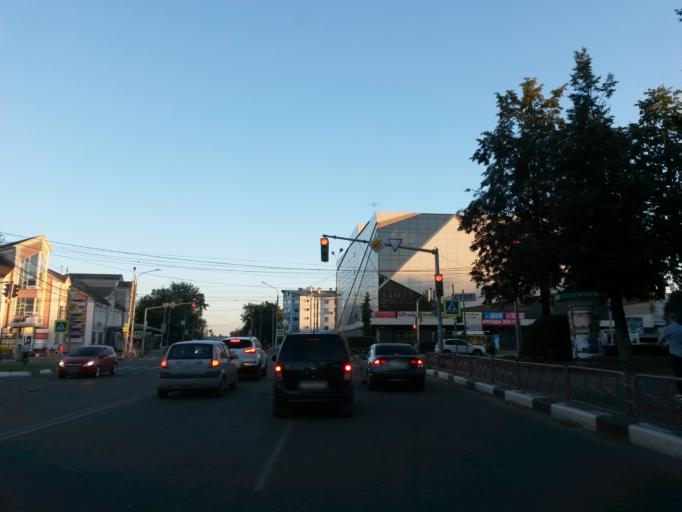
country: RU
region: Jaroslavl
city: Yaroslavl
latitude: 57.6265
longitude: 39.8679
